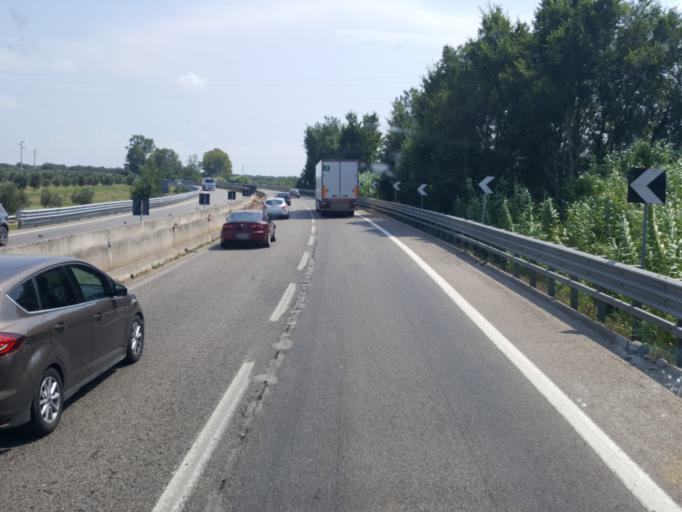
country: IT
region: Apulia
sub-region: Provincia di Brindisi
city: San Pietro Vernotico
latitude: 40.5075
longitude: 18.0243
